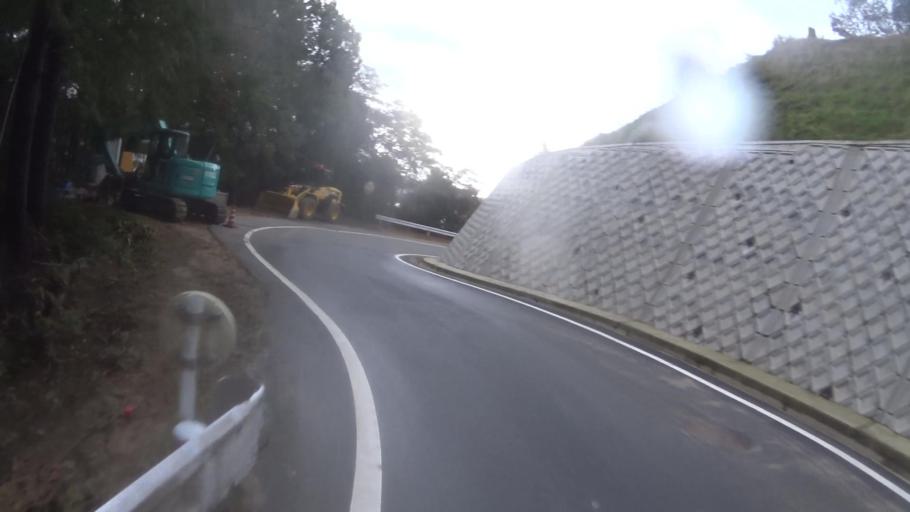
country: JP
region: Kyoto
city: Miyazu
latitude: 35.5293
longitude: 135.2317
